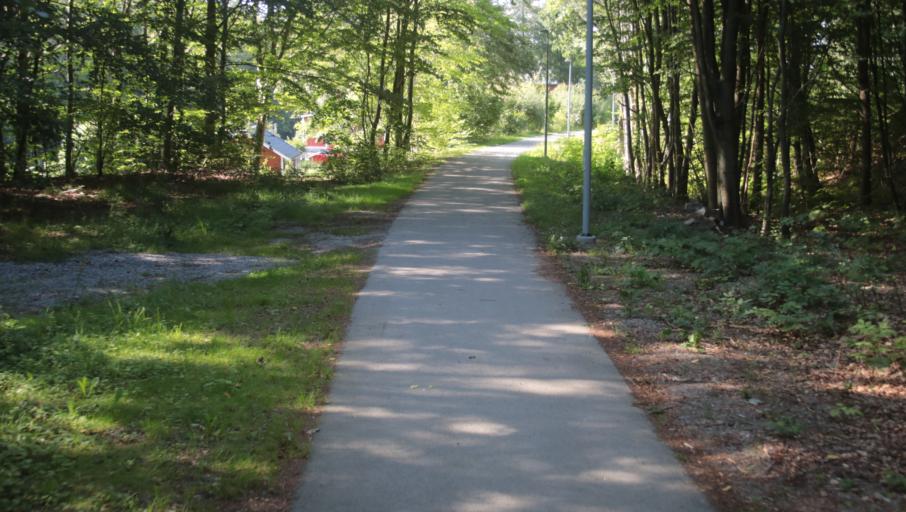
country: SE
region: Blekinge
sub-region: Karlshamns Kommun
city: Svangsta
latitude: 56.2562
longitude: 14.7764
